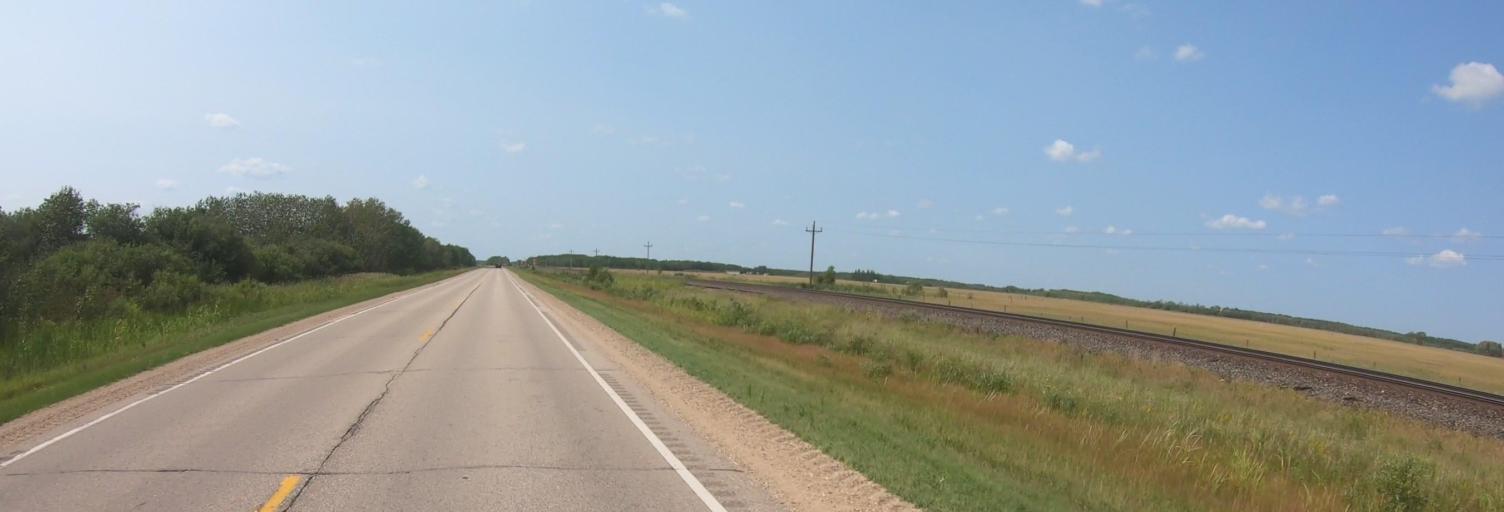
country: US
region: Minnesota
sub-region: Lake of the Woods County
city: Baudette
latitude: 48.7349
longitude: -94.8144
